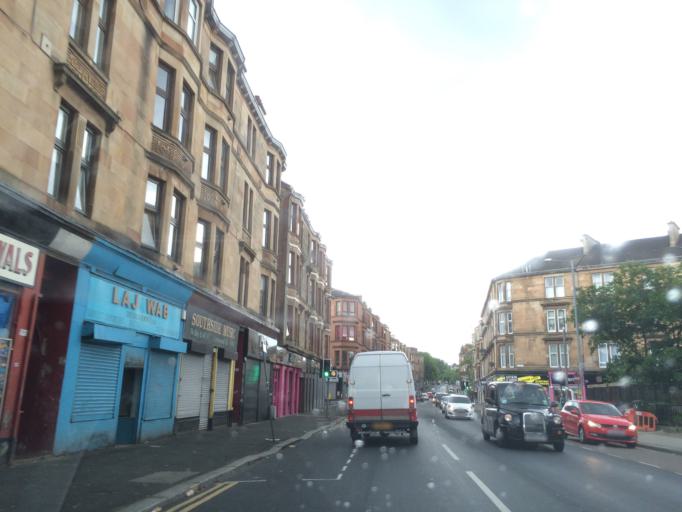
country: GB
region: Scotland
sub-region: Glasgow City
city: Glasgow
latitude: 55.8357
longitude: -4.2567
